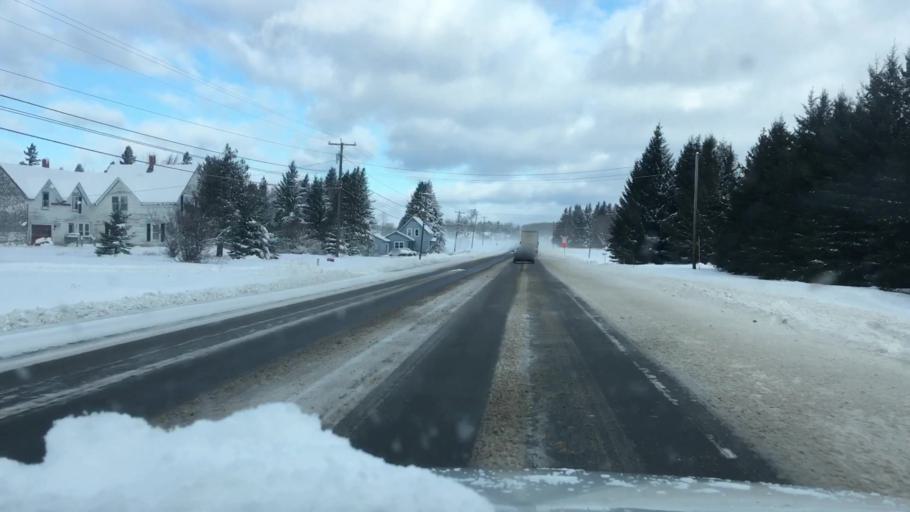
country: US
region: Maine
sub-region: Aroostook County
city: Caribou
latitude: 46.8053
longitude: -67.9934
